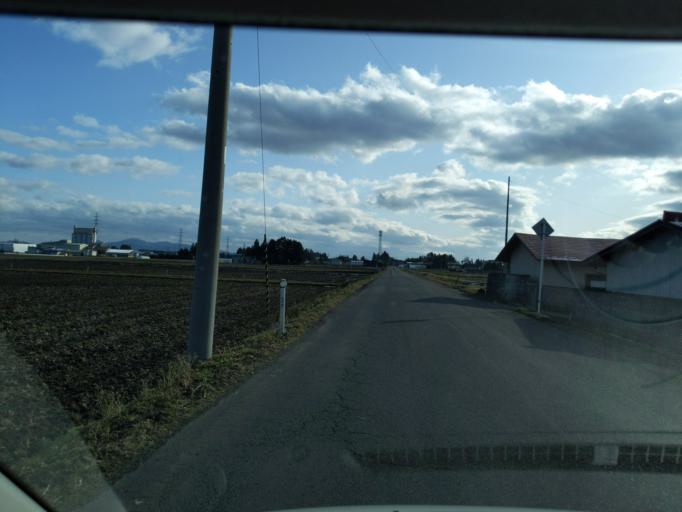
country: JP
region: Iwate
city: Mizusawa
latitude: 39.1453
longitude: 141.0789
